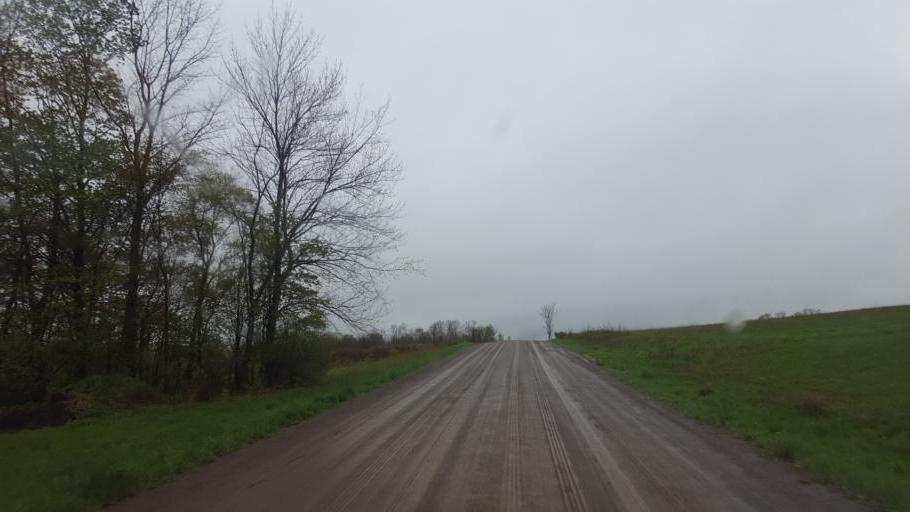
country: US
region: Pennsylvania
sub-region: Tioga County
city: Elkland
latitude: 42.0596
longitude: -77.4183
